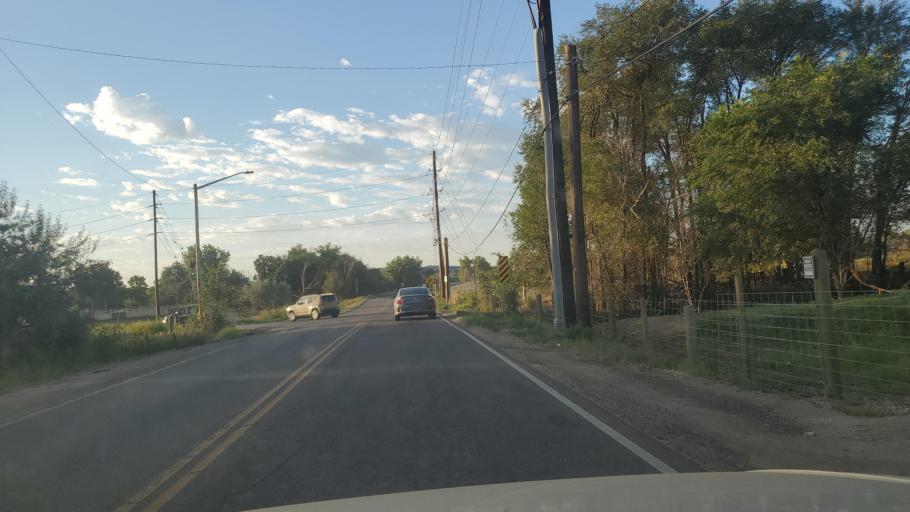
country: US
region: Colorado
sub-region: Adams County
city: Derby
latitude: 39.8712
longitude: -104.9116
